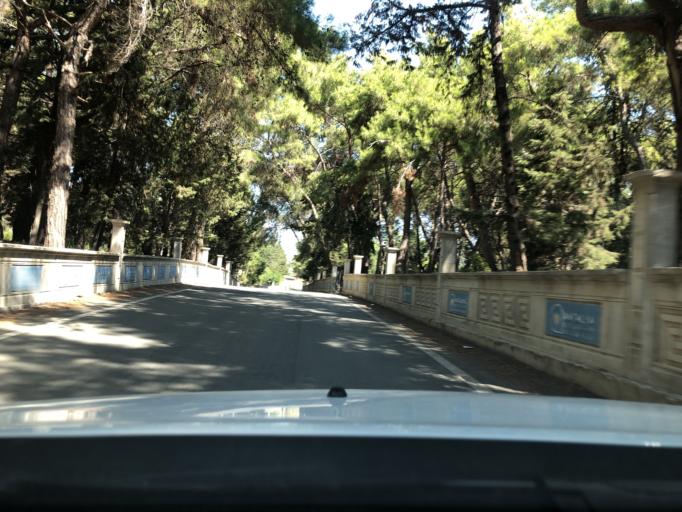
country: TR
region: Antalya
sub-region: Manavgat
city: Manavgat
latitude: 36.8154
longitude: 31.4890
